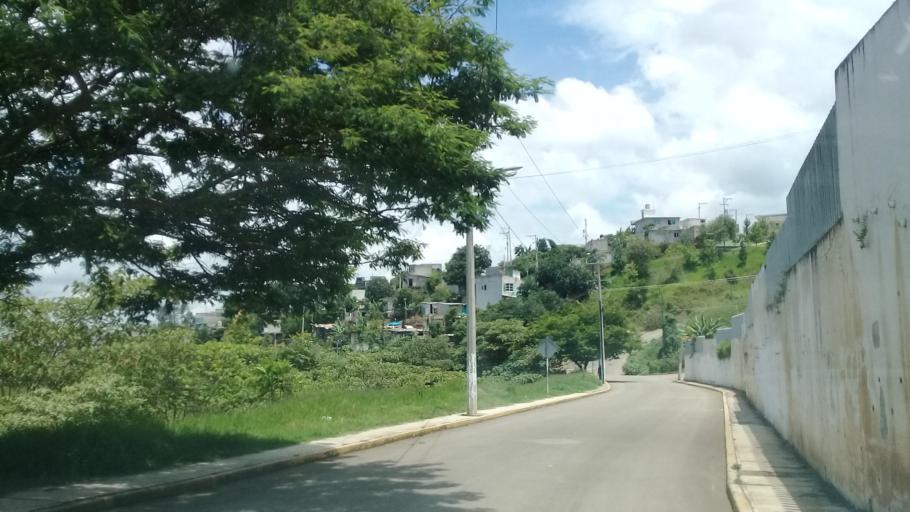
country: MX
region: Veracruz
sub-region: Xalapa
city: Fraccionamiento las Fuentes
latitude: 19.4990
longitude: -96.8825
